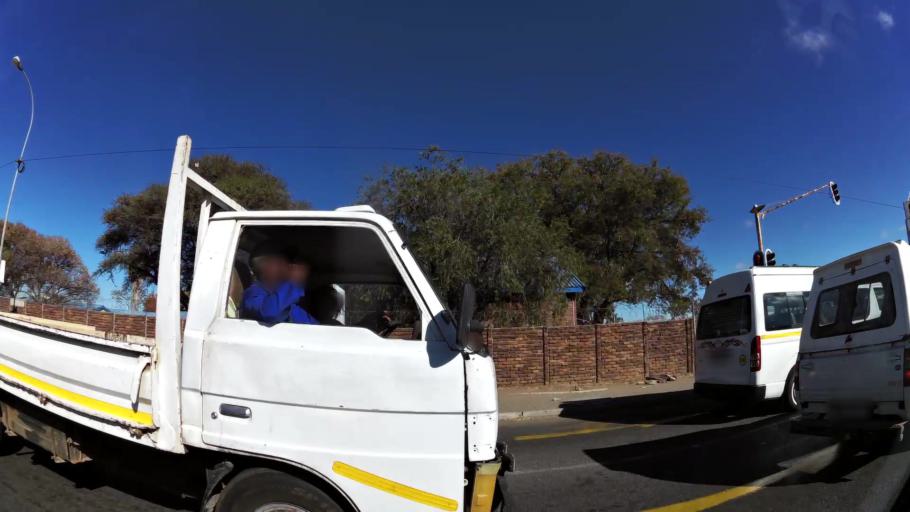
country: ZA
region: Limpopo
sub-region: Capricorn District Municipality
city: Polokwane
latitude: -23.8985
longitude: 29.4491
